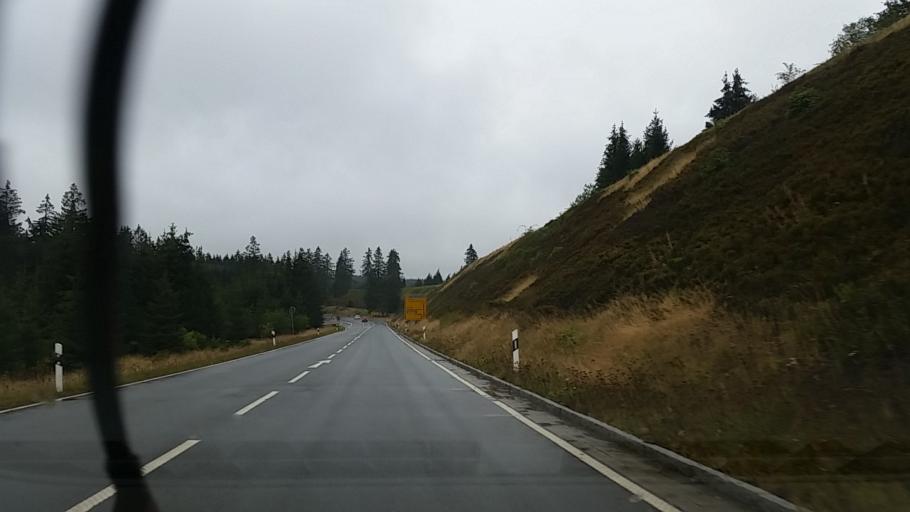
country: DE
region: Lower Saxony
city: Altenau
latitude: 51.7797
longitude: 10.4203
